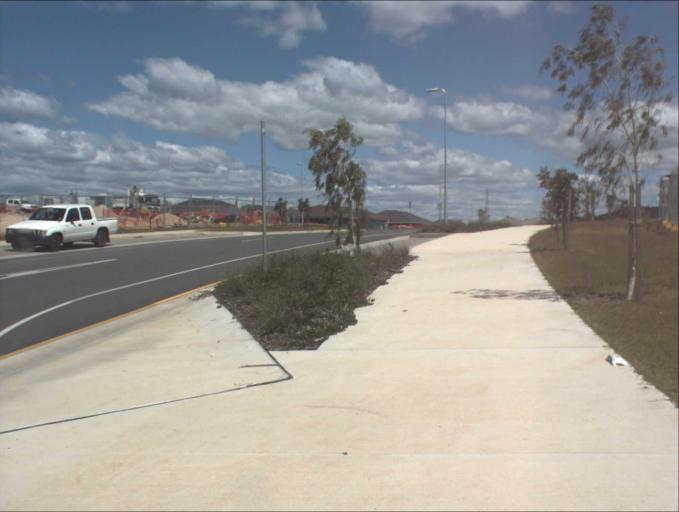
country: AU
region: Queensland
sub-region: Logan
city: Chambers Flat
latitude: -27.8032
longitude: 153.1153
